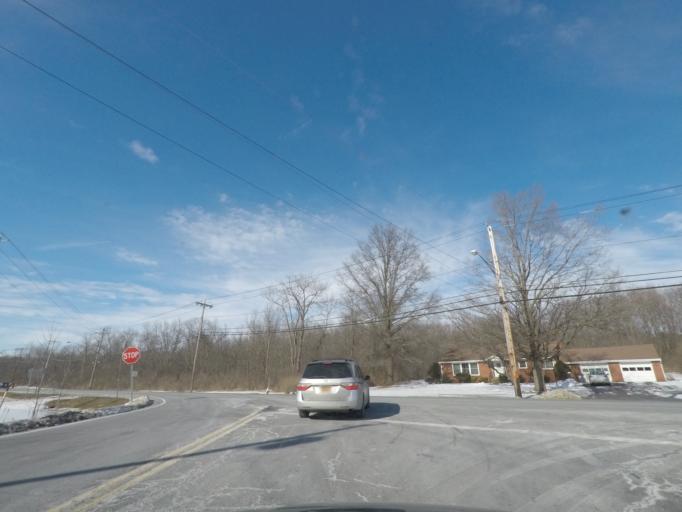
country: US
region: New York
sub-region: Albany County
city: Altamont
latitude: 42.7059
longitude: -73.9765
